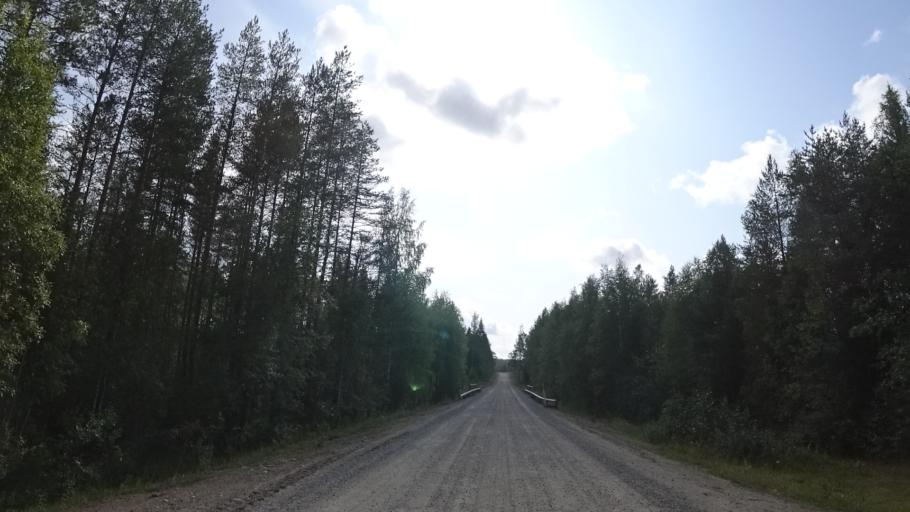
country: FI
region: North Karelia
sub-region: Pielisen Karjala
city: Lieksa
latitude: 63.5759
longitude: 30.1225
